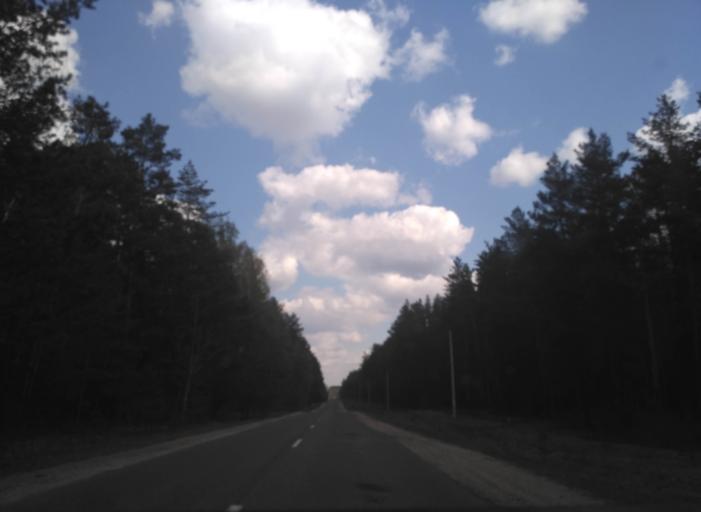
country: BY
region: Minsk
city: Radashkovichy
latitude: 54.1867
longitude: 27.2584
